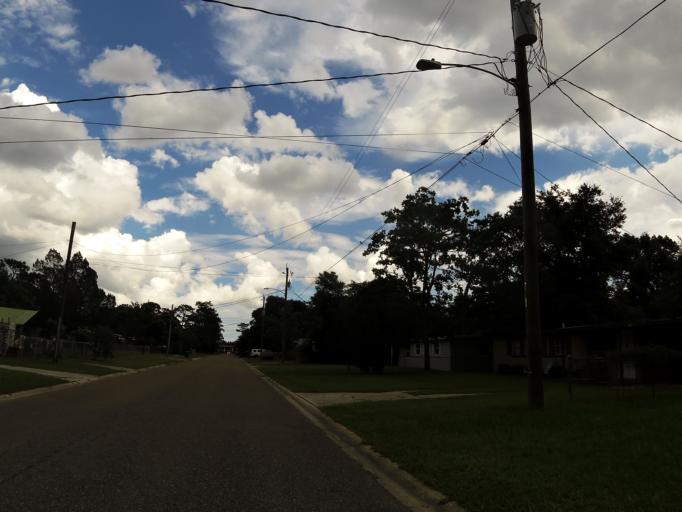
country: US
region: Florida
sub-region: Duval County
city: Jacksonville
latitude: 30.4249
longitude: -81.6636
